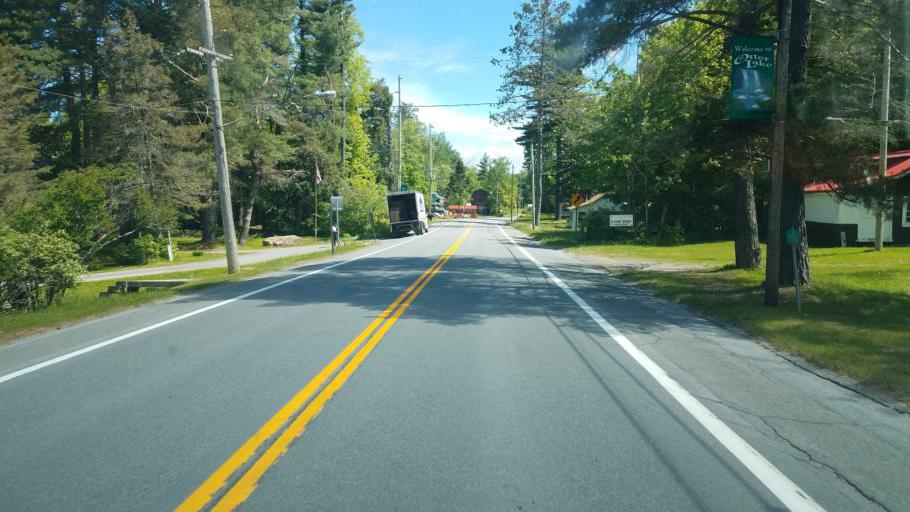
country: US
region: New York
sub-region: Oneida County
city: Boonville
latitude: 43.5894
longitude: -75.1132
